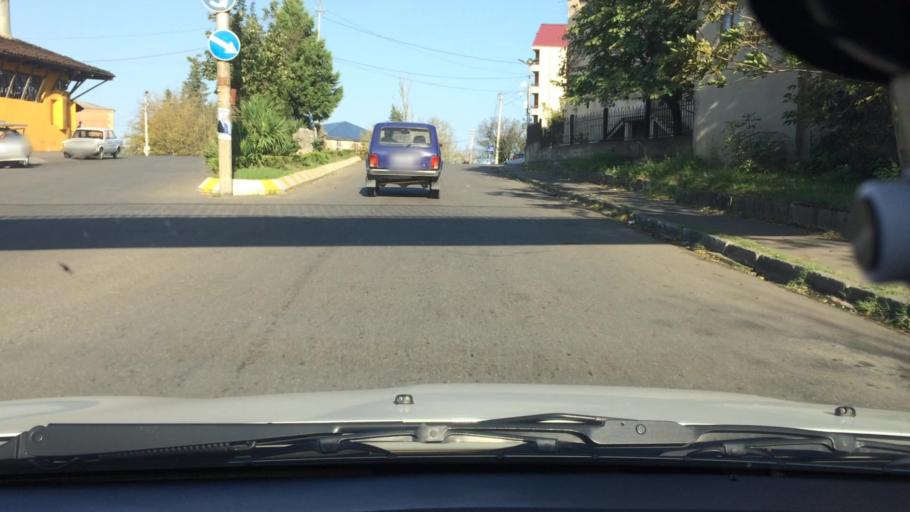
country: GE
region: Imereti
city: Kutaisi
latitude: 42.2657
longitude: 42.7191
